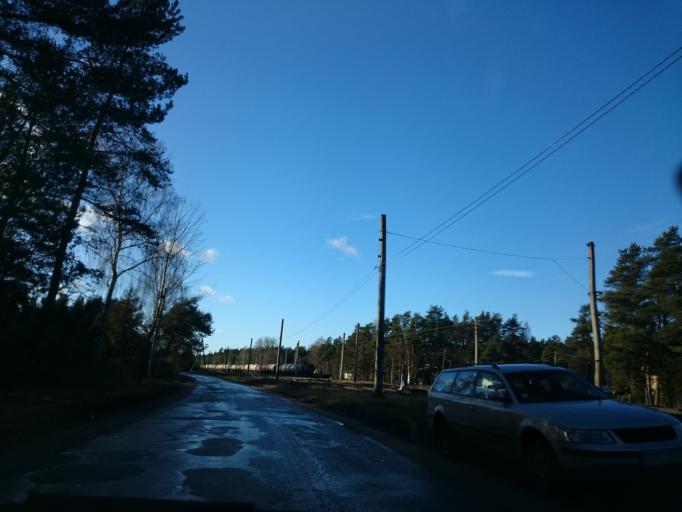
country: LV
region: Garkalne
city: Garkalne
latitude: 57.0488
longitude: 24.4219
